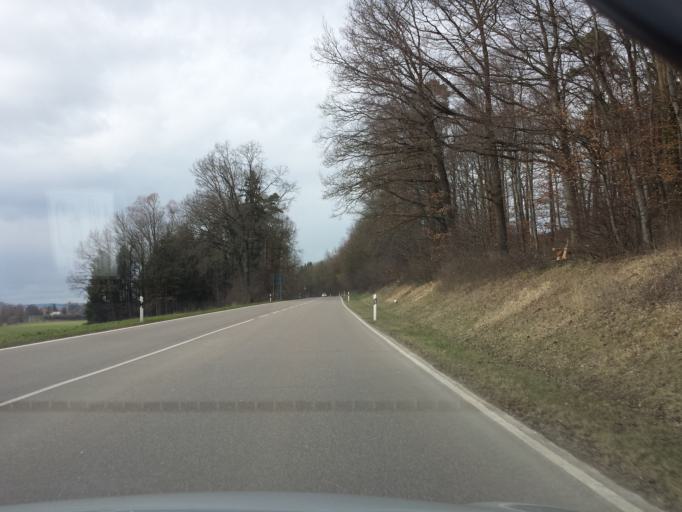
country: DE
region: Baden-Wuerttemberg
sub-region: Tuebingen Region
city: Achstetten
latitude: 48.2535
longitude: 9.9130
